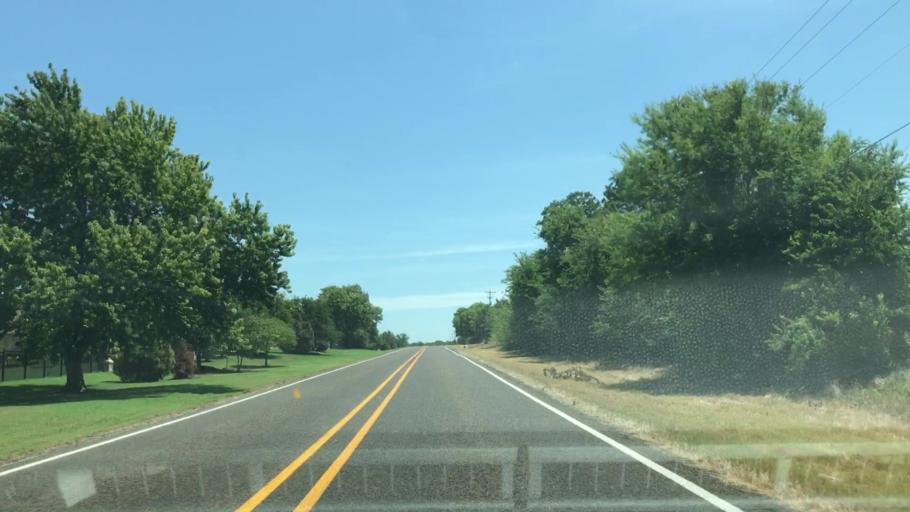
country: US
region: Texas
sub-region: Collin County
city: Fairview
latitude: 33.1562
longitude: -96.6203
